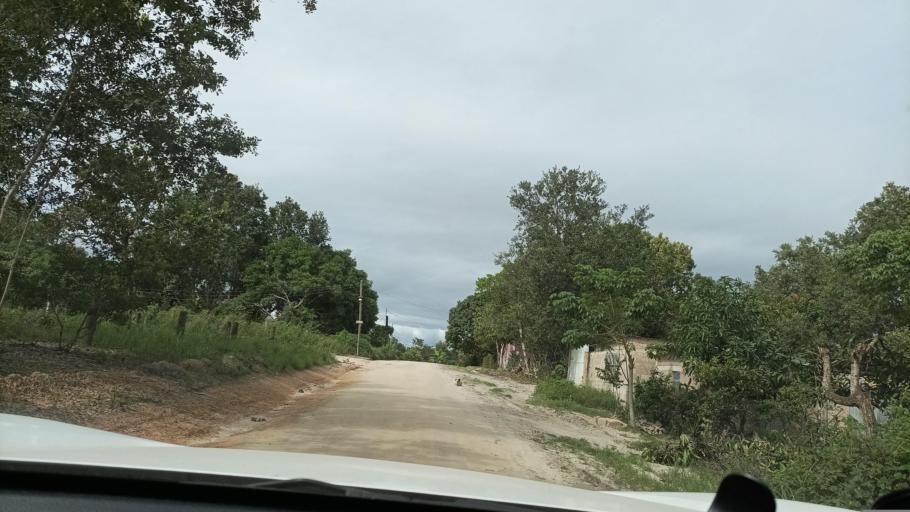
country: MX
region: Veracruz
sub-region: Cosoleacaque
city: Coacotla
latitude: 17.9469
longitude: -94.7104
